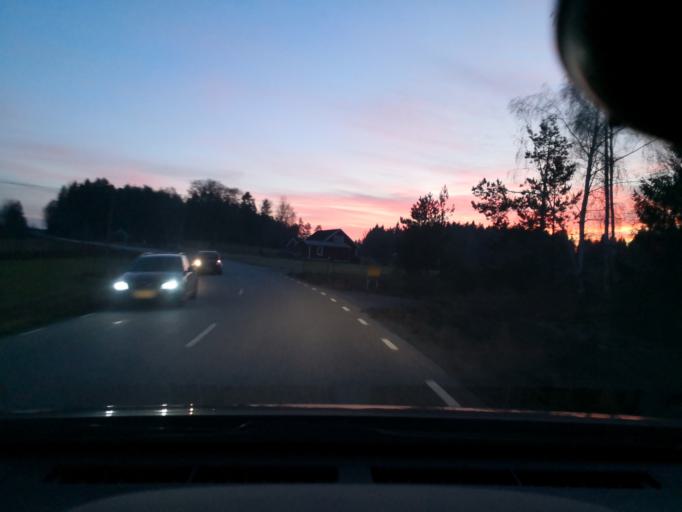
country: SE
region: OErebro
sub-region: Lindesbergs Kommun
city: Frovi
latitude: 59.3707
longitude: 15.4311
